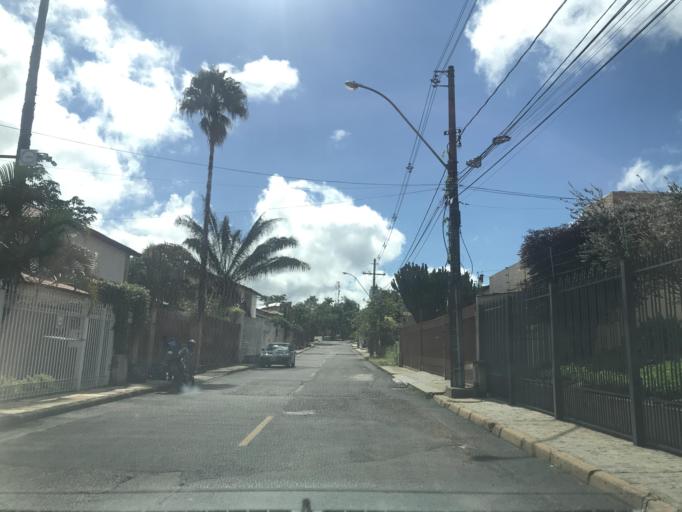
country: BR
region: Federal District
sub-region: Brasilia
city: Brasilia
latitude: -15.7231
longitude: -47.8776
